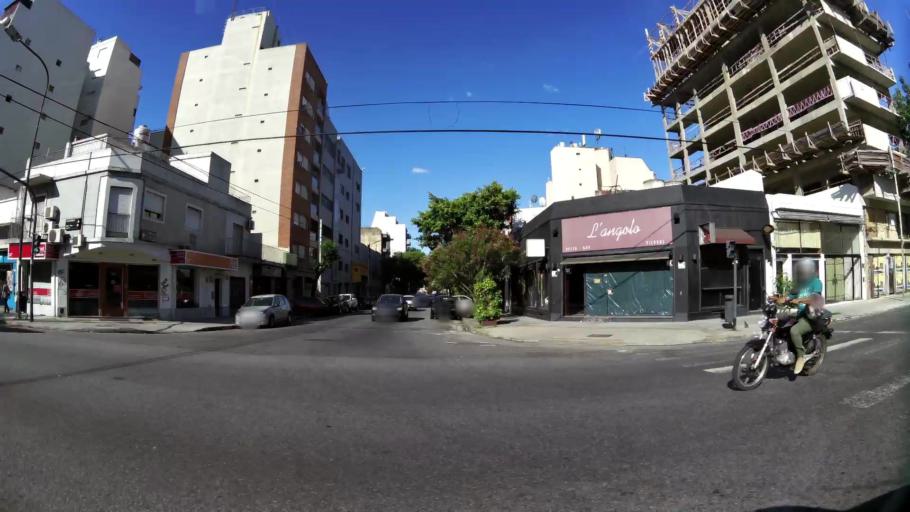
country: AR
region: Buenos Aires F.D.
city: Villa Santa Rita
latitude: -34.6173
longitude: -58.4762
